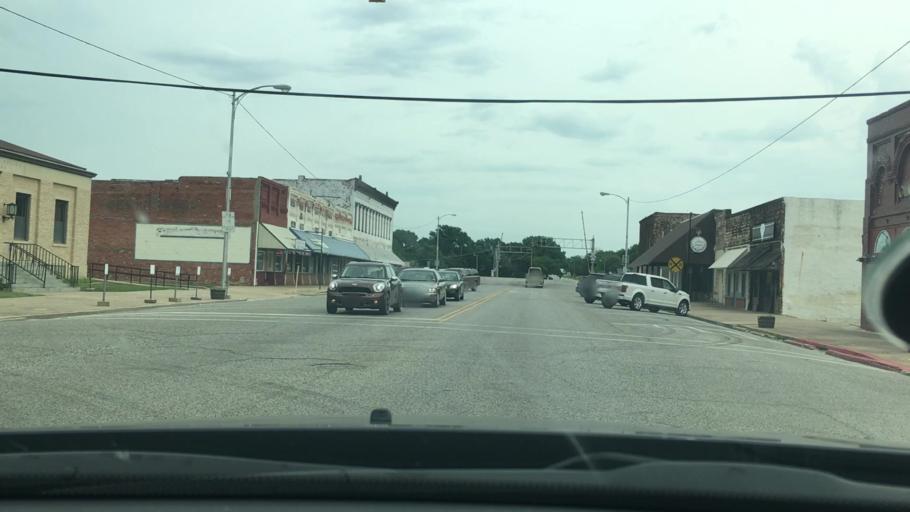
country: US
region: Oklahoma
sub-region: Love County
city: Marietta
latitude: 33.9372
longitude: -97.1182
